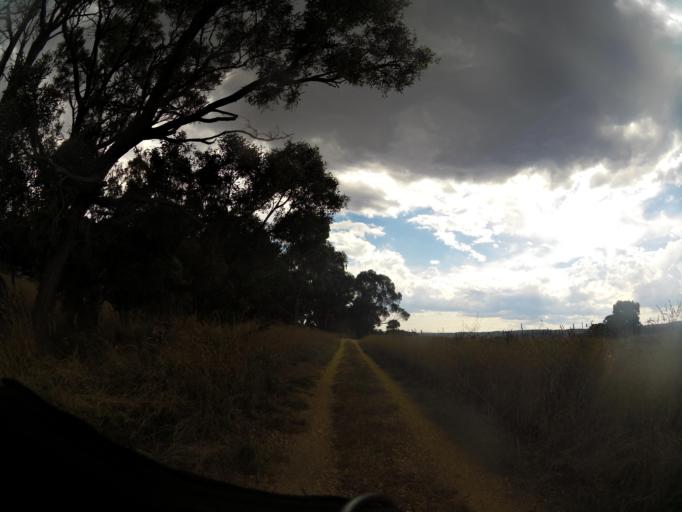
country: AU
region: Victoria
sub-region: Wellington
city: Heyfield
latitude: -38.0169
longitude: 146.6875
